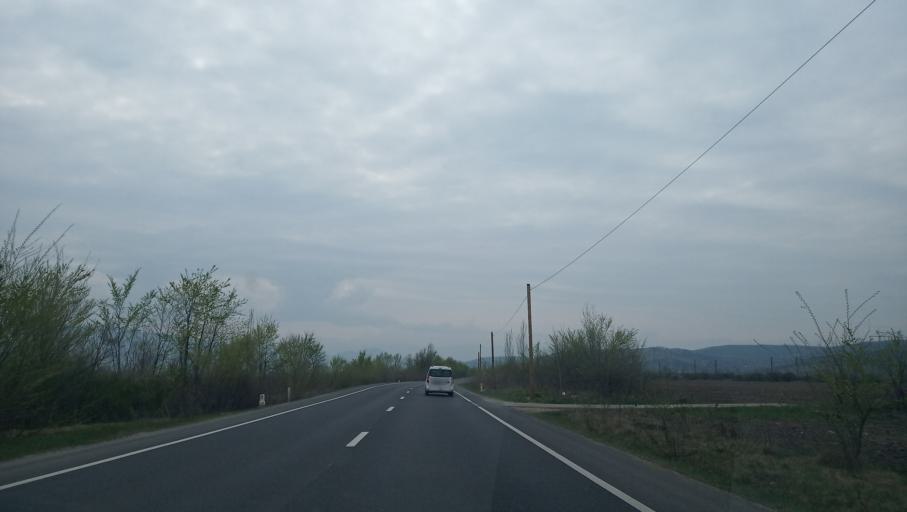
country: RO
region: Hunedoara
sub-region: Comuna Bretea Romana
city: Bretea Romana
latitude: 45.6900
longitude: 22.9921
